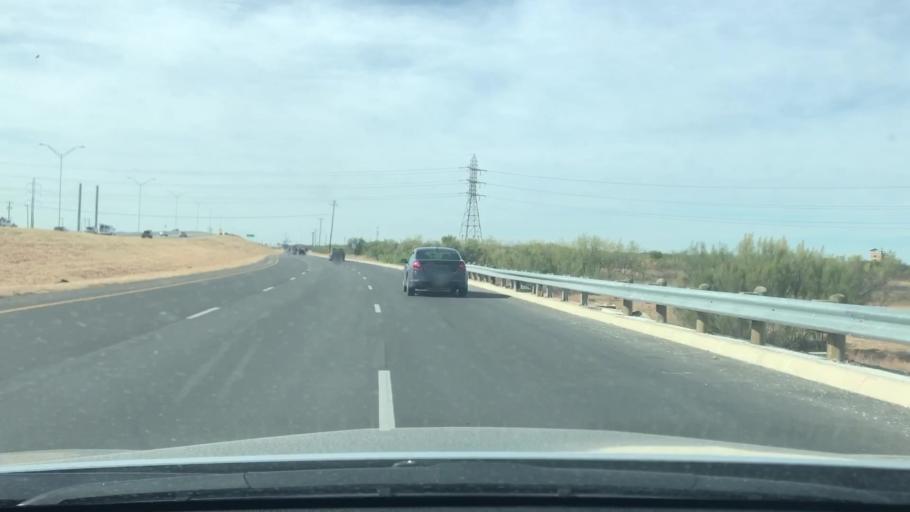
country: US
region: Texas
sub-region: Bexar County
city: Lackland Air Force Base
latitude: 29.4247
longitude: -98.5944
